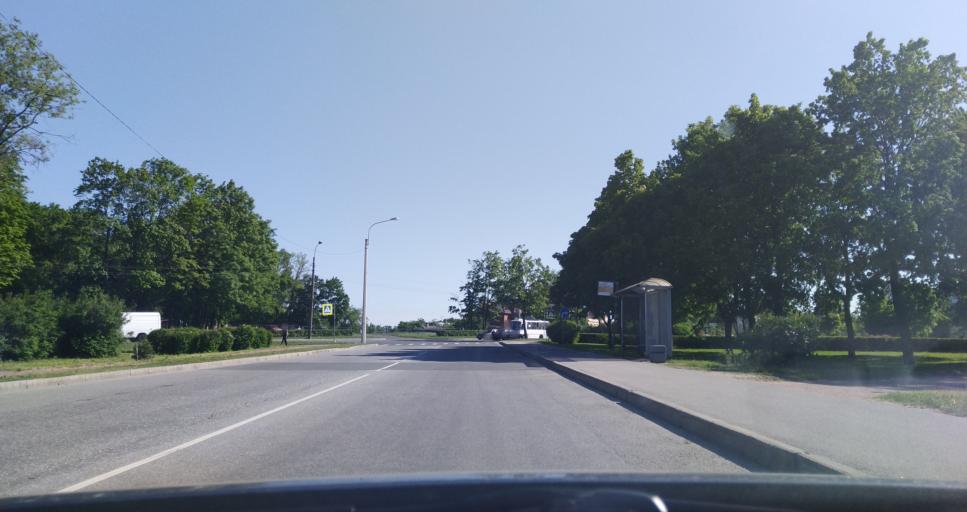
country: RU
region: St.-Petersburg
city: Krasnoye Selo
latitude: 59.7419
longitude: 30.0928
